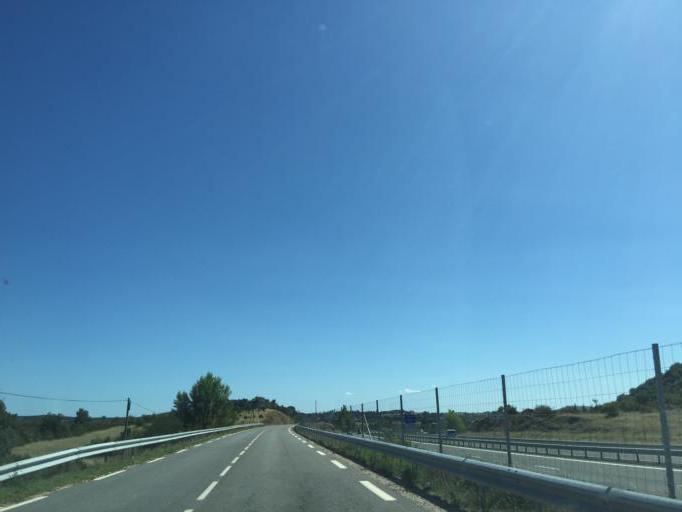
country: FR
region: Languedoc-Roussillon
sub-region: Departement de l'Herault
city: Lodeve
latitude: 43.8789
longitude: 3.3117
